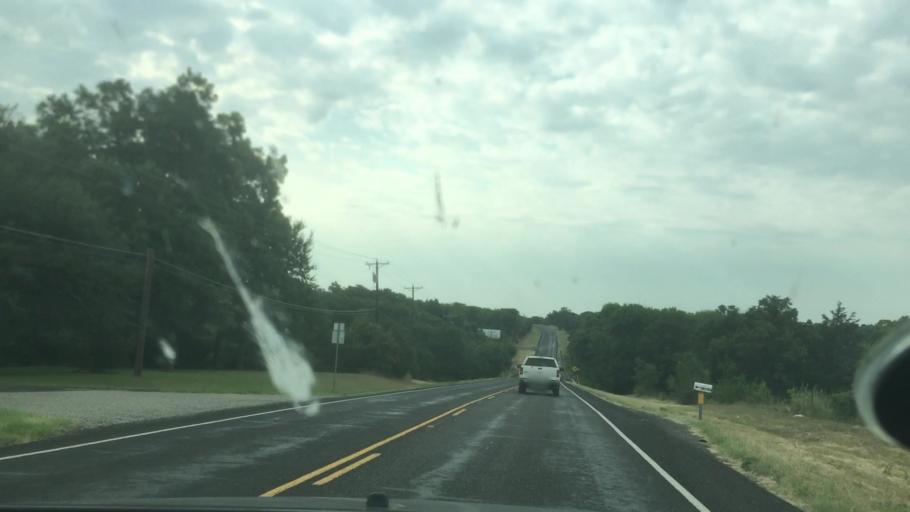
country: US
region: Texas
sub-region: Grayson County
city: Pottsboro
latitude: 33.7930
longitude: -96.6091
